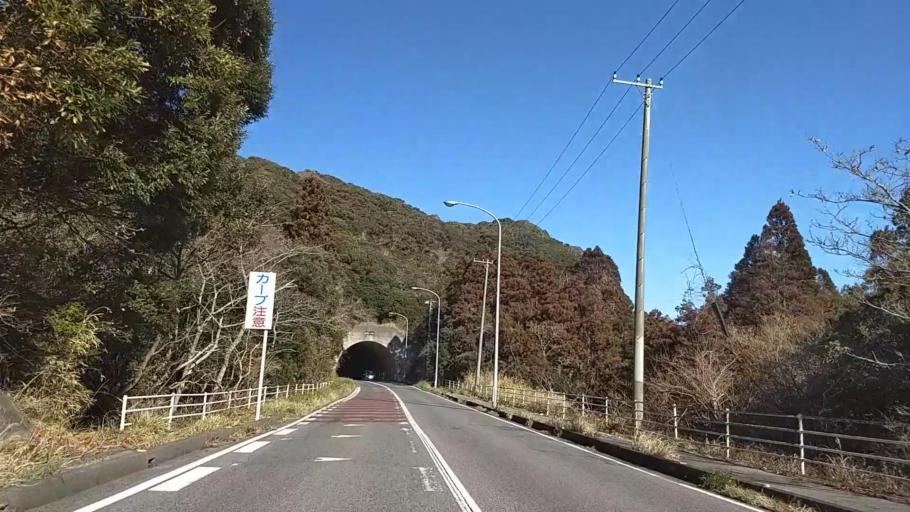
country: JP
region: Chiba
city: Katsuura
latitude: 35.1288
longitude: 140.2391
